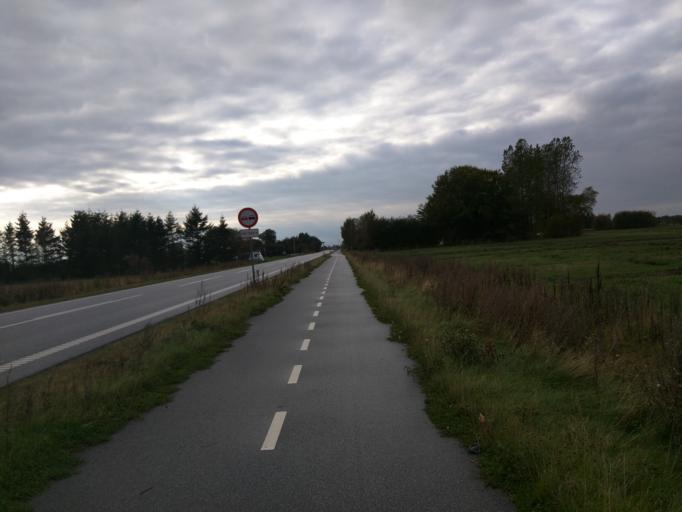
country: DK
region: Central Jutland
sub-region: Viborg Kommune
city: Bjerringbro
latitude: 56.4744
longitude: 9.5651
